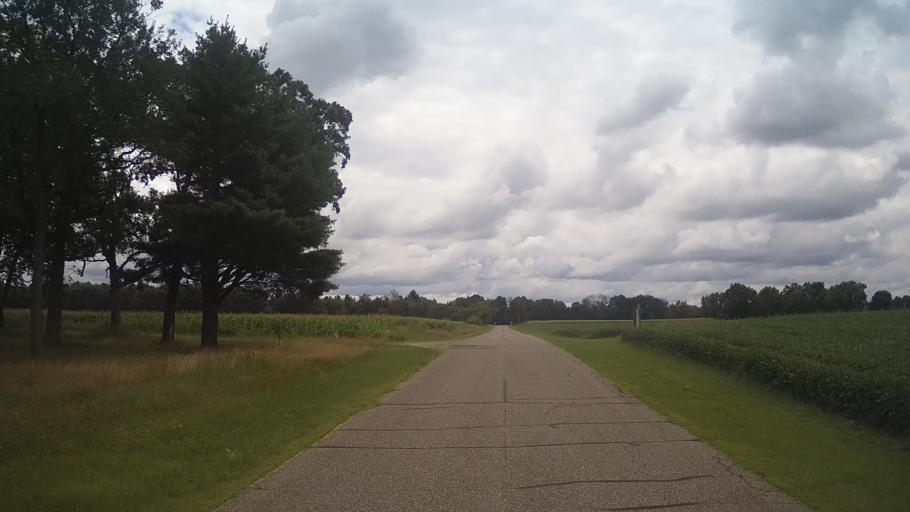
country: US
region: Wisconsin
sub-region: Adams County
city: Friendship
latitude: 44.0289
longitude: -89.9177
